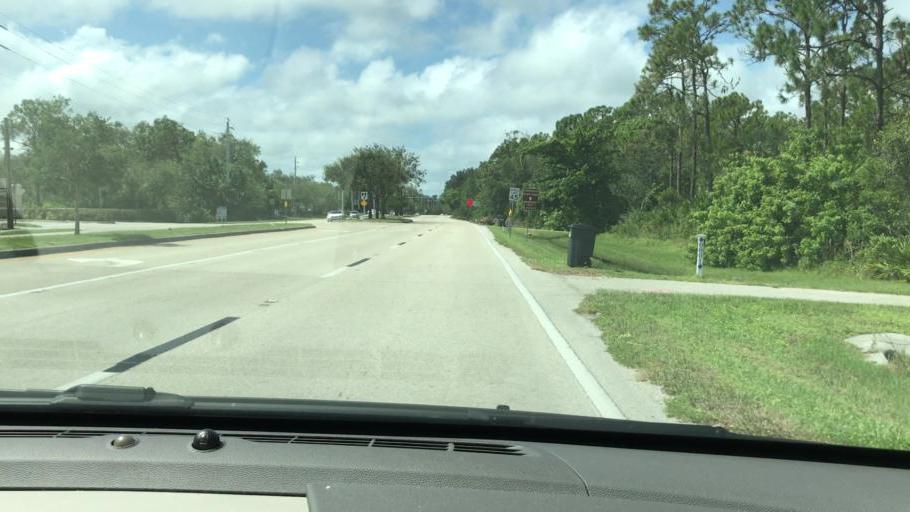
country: US
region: Florida
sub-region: Lee County
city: Estero
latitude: 26.4314
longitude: -81.8073
